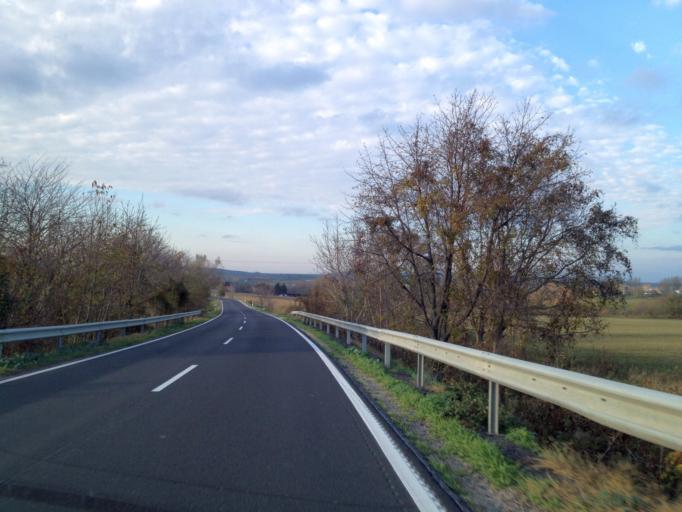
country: HU
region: Gyor-Moson-Sopron
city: Bakonyszentlaszlo
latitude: 47.4247
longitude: 17.8405
